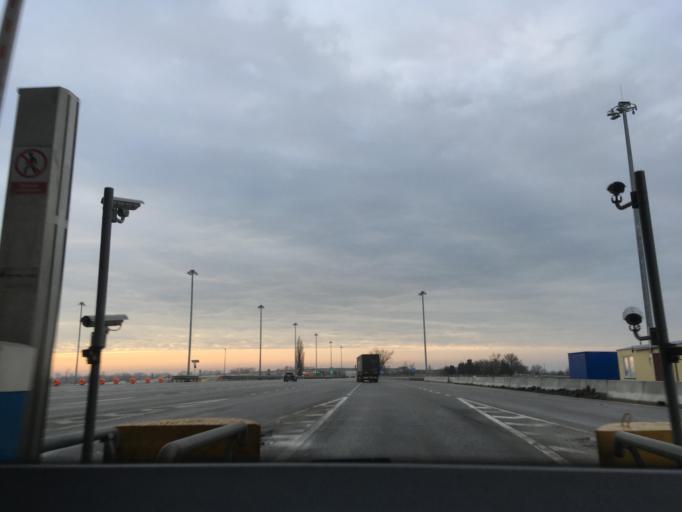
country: RU
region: Krasnodarskiy
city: Pavlovskaya
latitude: 46.2304
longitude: 39.8310
